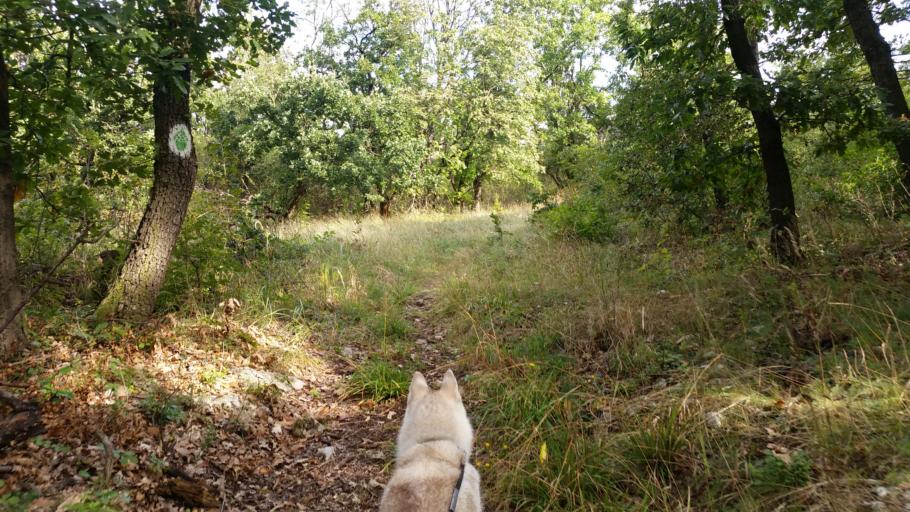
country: HU
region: Pest
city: Telki
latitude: 47.5641
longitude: 18.8303
